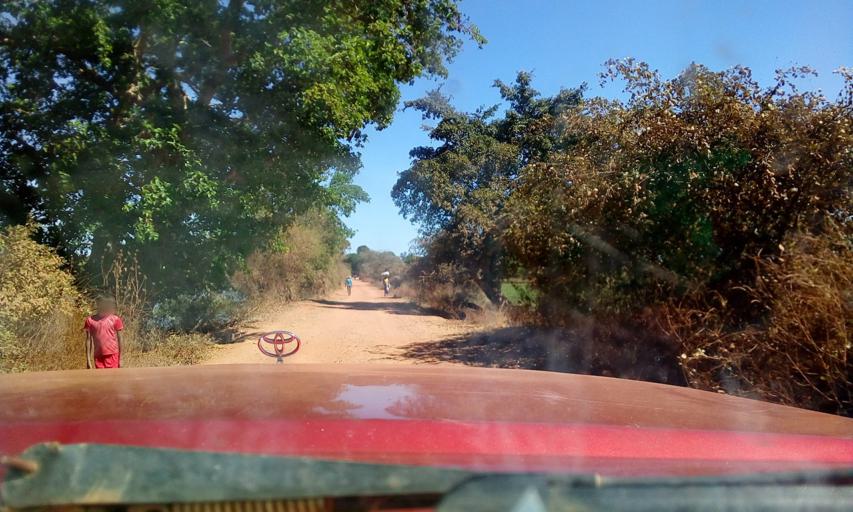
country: MG
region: Boeny
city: Mahajanga
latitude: -15.9611
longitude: 45.9518
